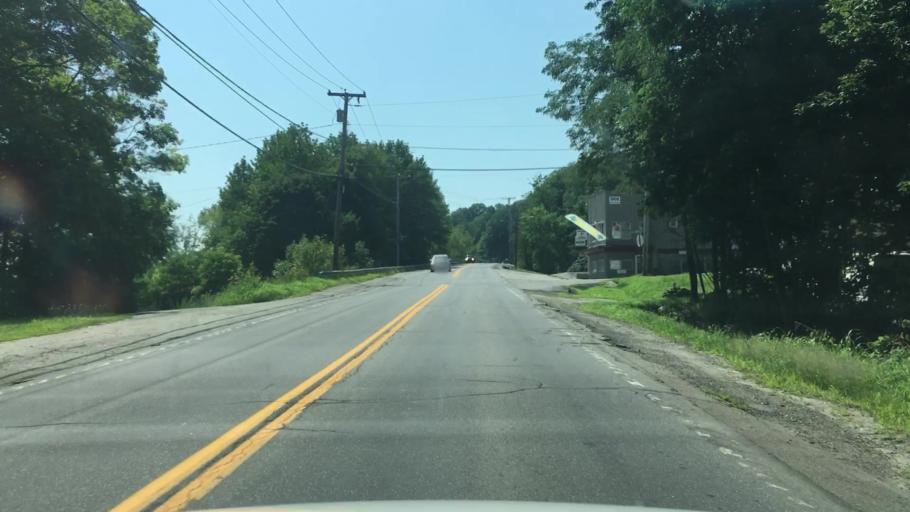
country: US
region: Maine
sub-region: Kennebec County
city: Hallowell
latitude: 44.2758
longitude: -69.7919
